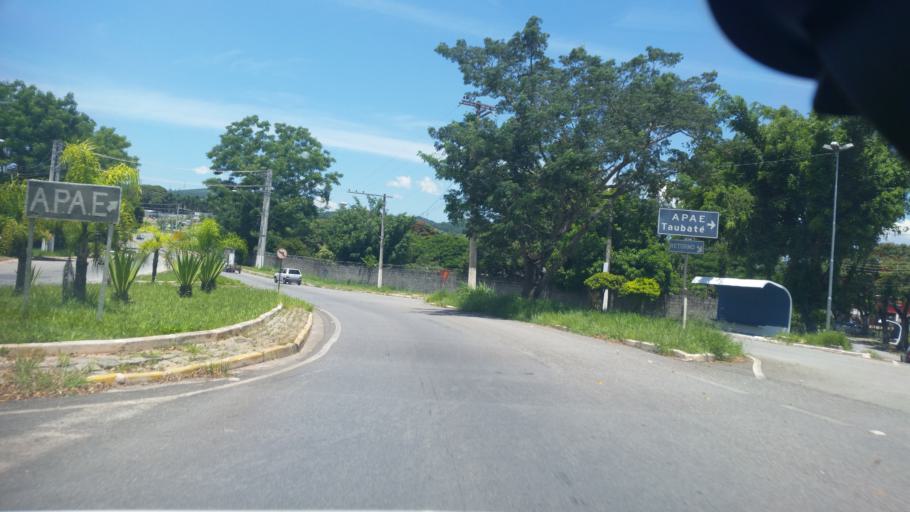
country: BR
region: Sao Paulo
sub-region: Taubate
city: Taubate
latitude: -23.0685
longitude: -45.5562
